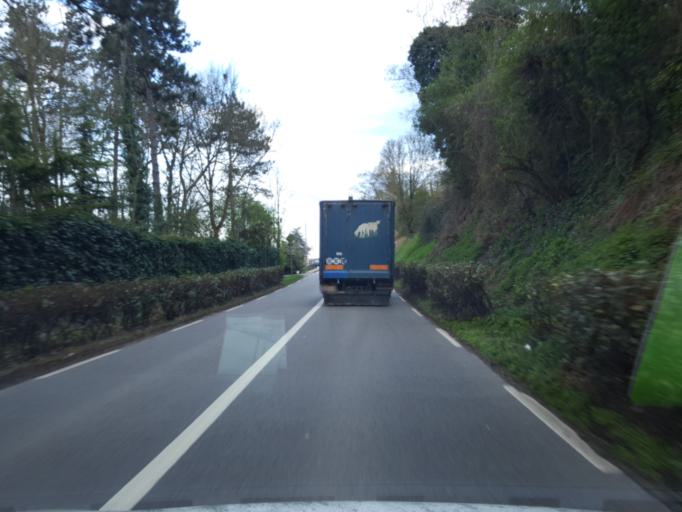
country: FR
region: Ile-de-France
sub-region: Departement des Yvelines
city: Magnanville
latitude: 48.9457
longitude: 1.6948
